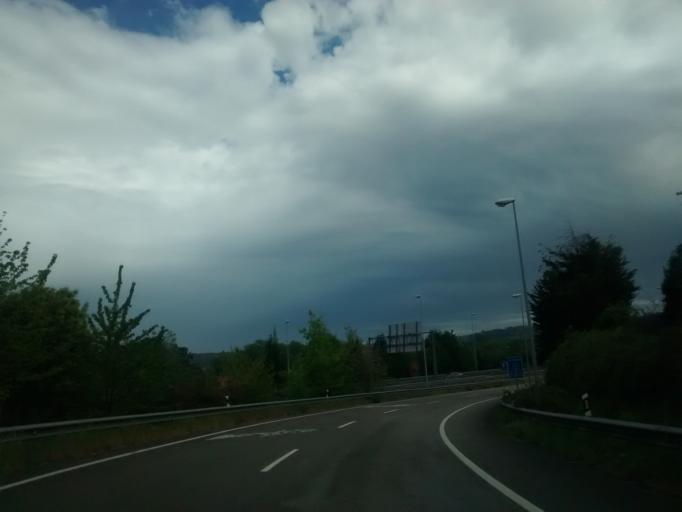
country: ES
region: Asturias
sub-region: Province of Asturias
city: Gijon
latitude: 43.5204
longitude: -5.6355
